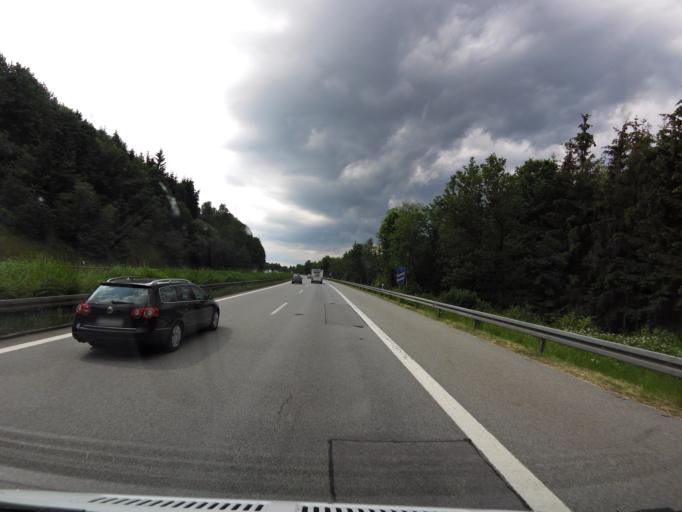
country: DE
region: Bavaria
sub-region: Lower Bavaria
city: Aussernzell
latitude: 48.6837
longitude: 13.2169
